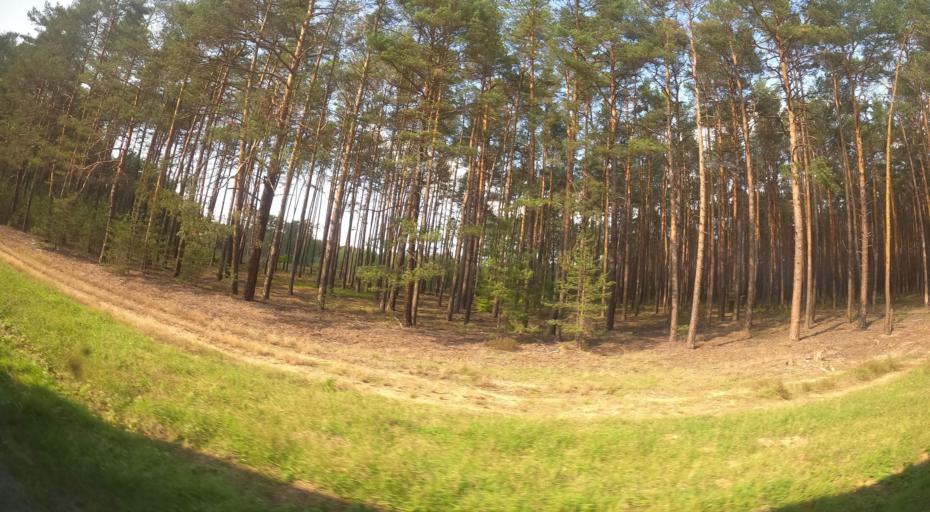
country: PL
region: Lubusz
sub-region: Powiat zielonogorski
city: Nowogrod Bobrzanski
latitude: 51.8594
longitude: 15.3010
